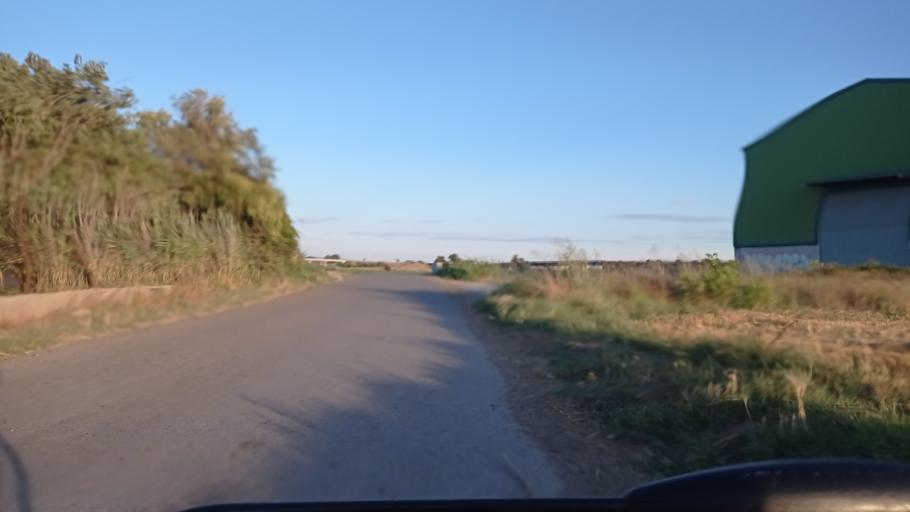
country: ES
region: Aragon
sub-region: Provincia de Zaragoza
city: Oliver-Valdefierro, Oliver, Valdefierro
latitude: 41.6813
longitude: -0.9337
